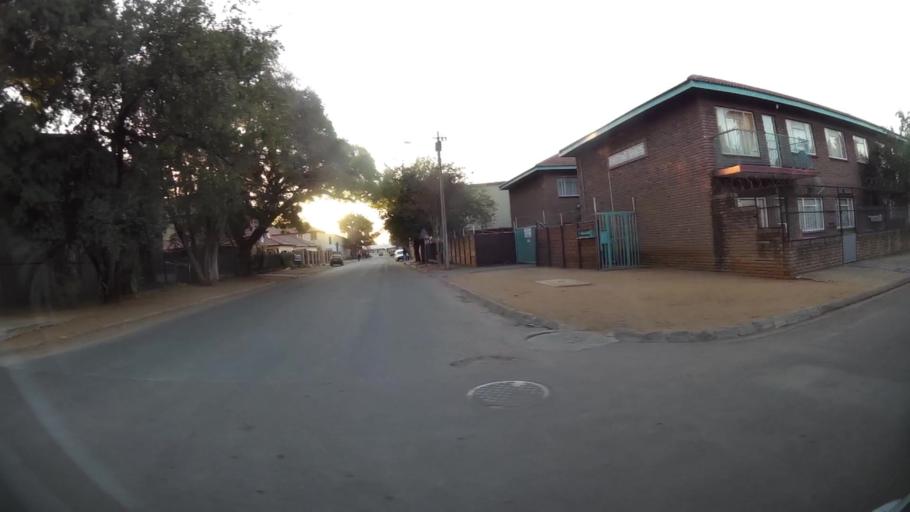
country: ZA
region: North-West
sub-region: Bojanala Platinum District Municipality
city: Rustenburg
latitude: -25.6649
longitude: 27.2468
